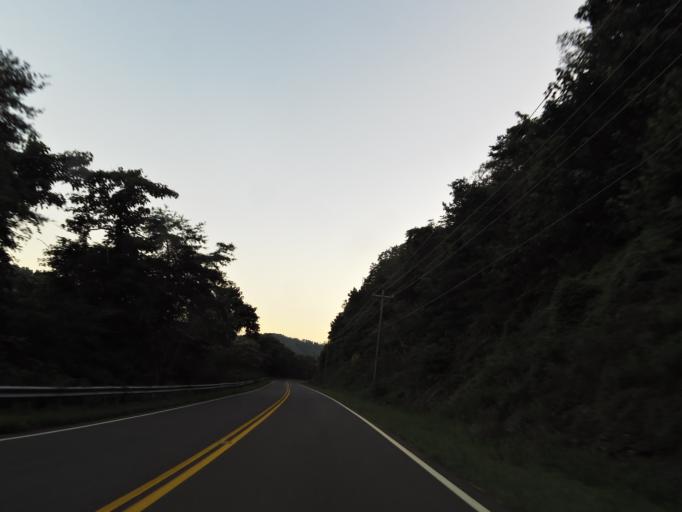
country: US
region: Tennessee
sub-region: Loudon County
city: Greenback
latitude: 35.5498
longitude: -84.0309
